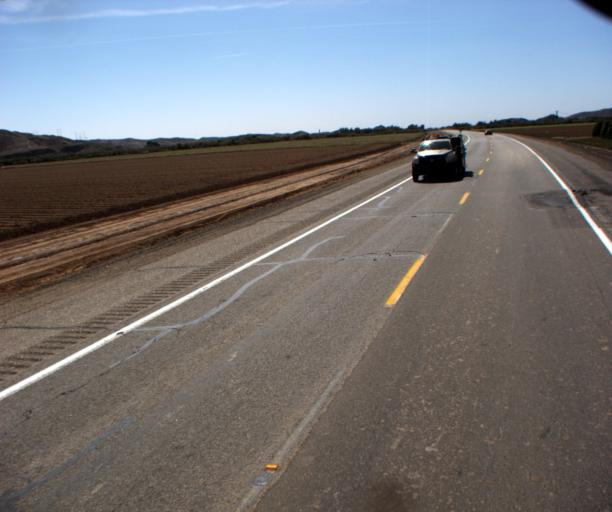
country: US
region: Arizona
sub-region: Yuma County
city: Fortuna Foothills
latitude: 32.7664
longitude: -114.4050
